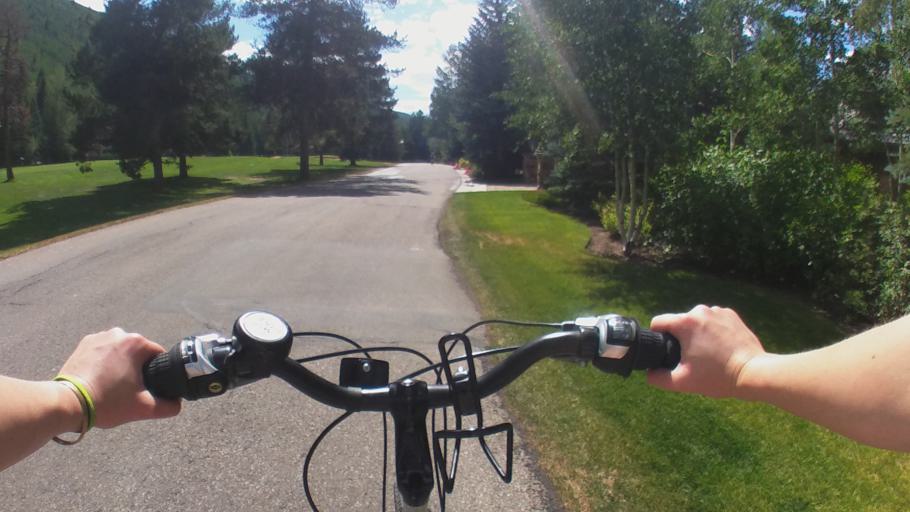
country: US
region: Colorado
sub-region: Summit County
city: Frisco
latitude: 39.5432
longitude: -106.2197
